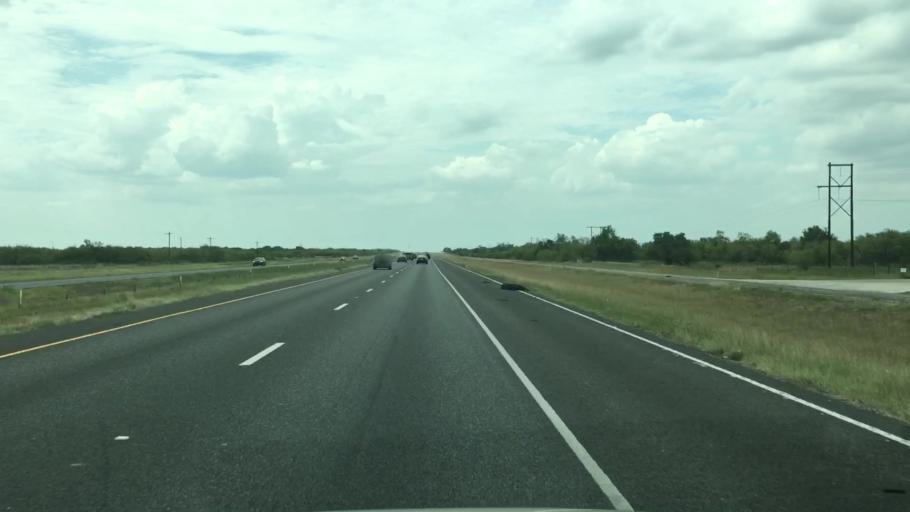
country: US
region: Texas
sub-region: Atascosa County
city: Pleasanton
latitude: 28.8008
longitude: -98.3417
